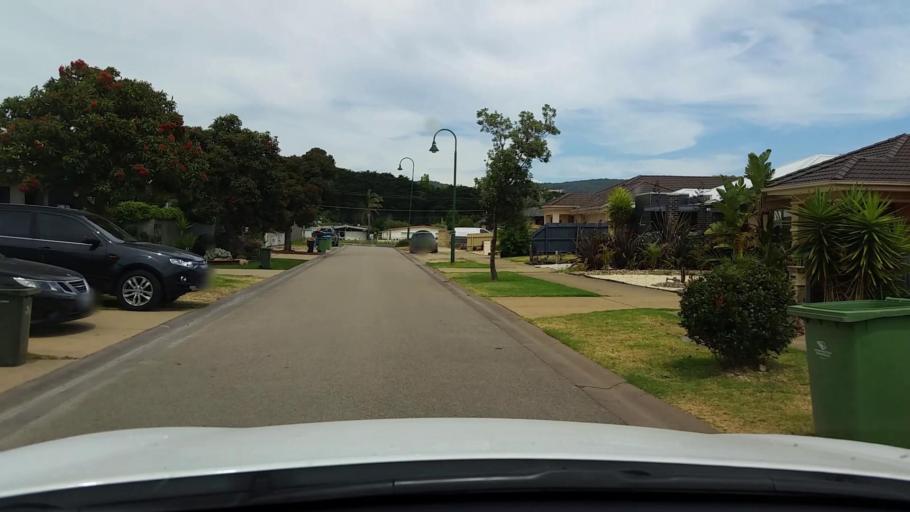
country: AU
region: Victoria
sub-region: Mornington Peninsula
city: Dromana
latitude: -38.3283
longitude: 144.9839
